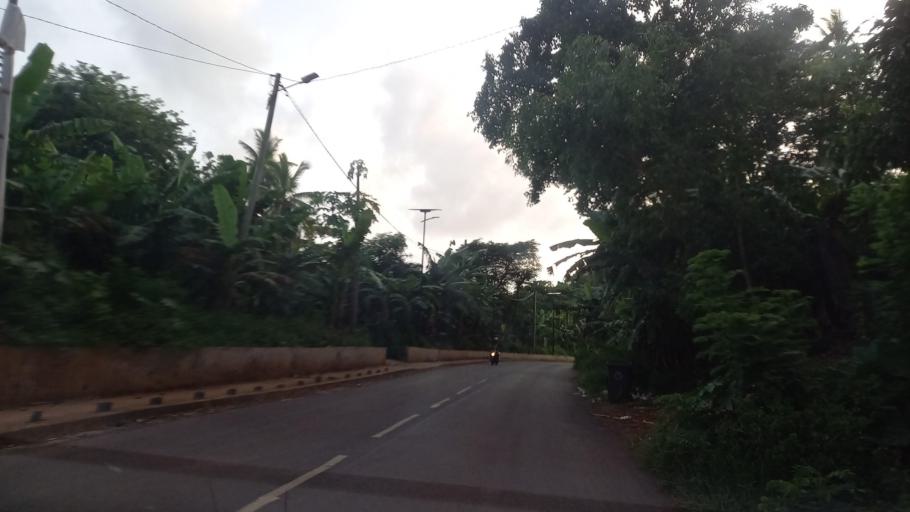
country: YT
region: M'Tsangamouji
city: M'Tsangamouji
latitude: -12.7629
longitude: 45.0817
